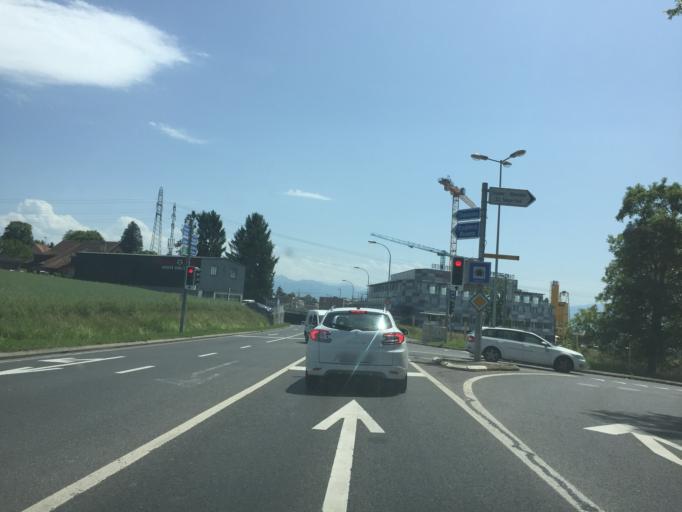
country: CH
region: Vaud
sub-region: Ouest Lausannois District
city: Crissier
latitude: 46.5507
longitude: 6.5746
